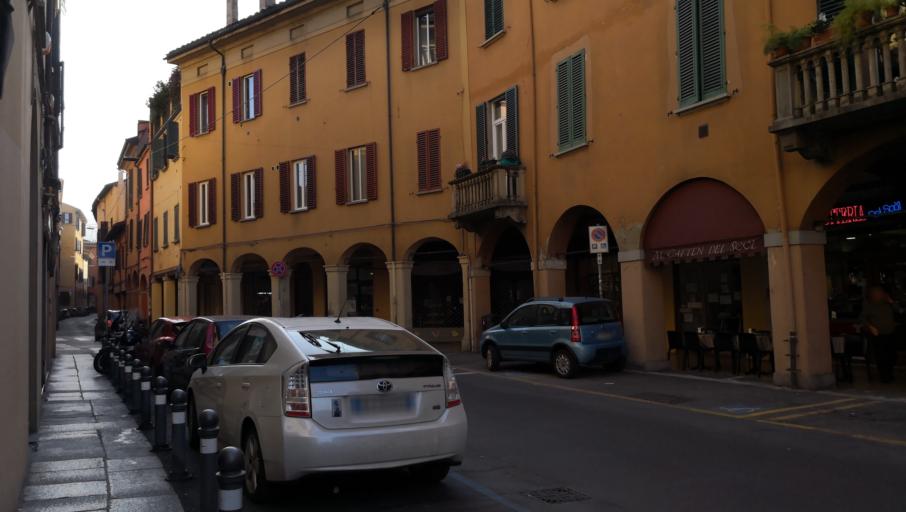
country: IT
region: Emilia-Romagna
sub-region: Provincia di Bologna
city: Bologna
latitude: 44.4931
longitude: 11.3358
